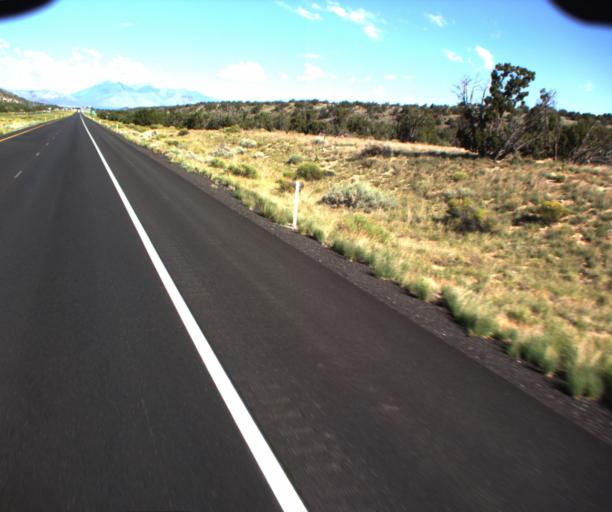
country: US
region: Arizona
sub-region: Coconino County
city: Flagstaff
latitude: 35.1910
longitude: -111.3802
